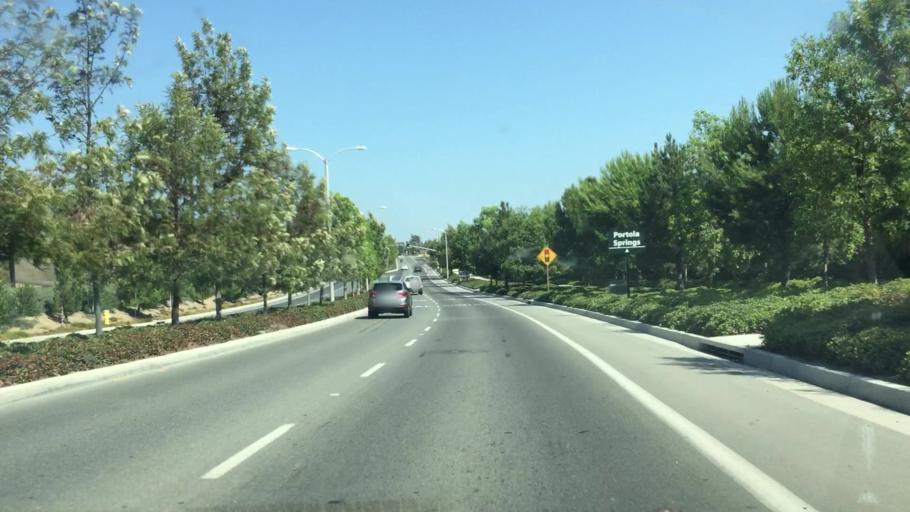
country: US
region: California
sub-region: Orange County
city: Lake Forest
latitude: 33.7082
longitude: -117.7344
